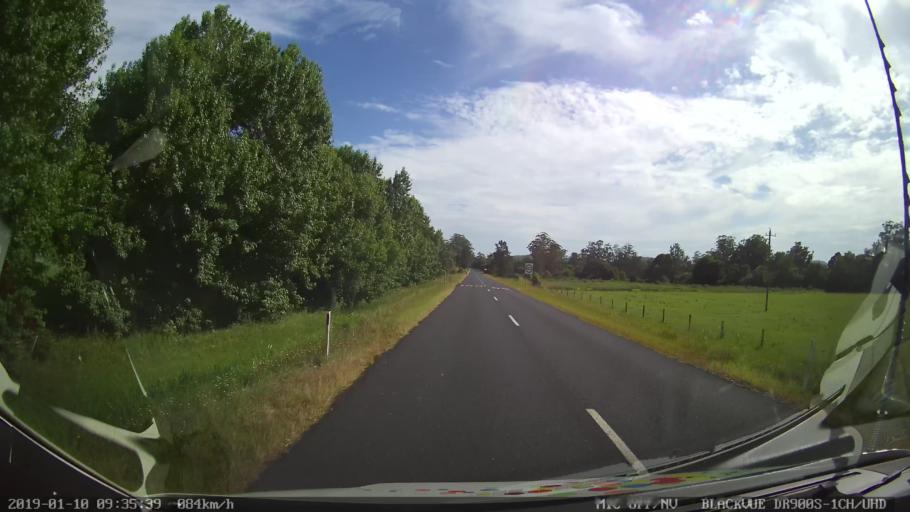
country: AU
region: New South Wales
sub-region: Coffs Harbour
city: Nana Glen
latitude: -30.2076
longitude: 153.0116
